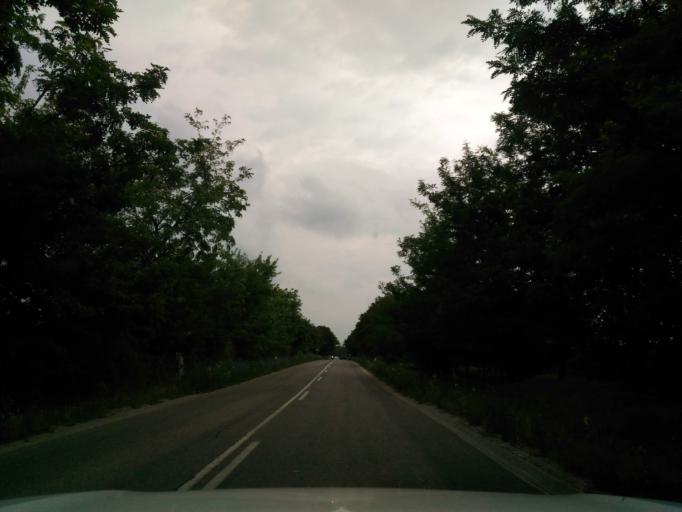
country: HU
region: Pest
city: Ujhartyan
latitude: 47.2082
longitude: 19.3687
